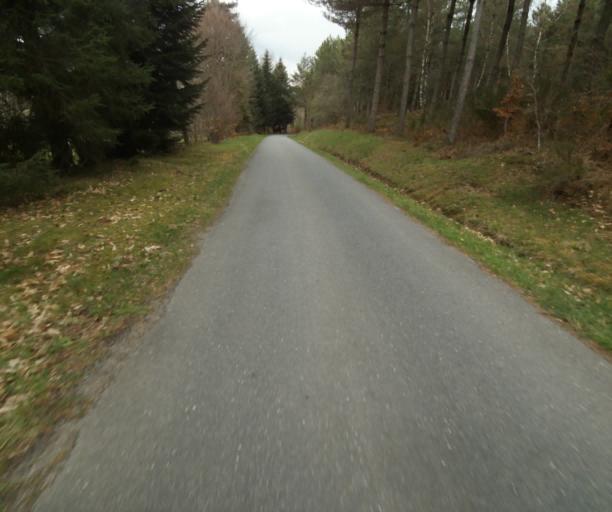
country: FR
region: Limousin
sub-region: Departement de la Correze
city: Correze
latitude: 45.3069
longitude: 1.9053
